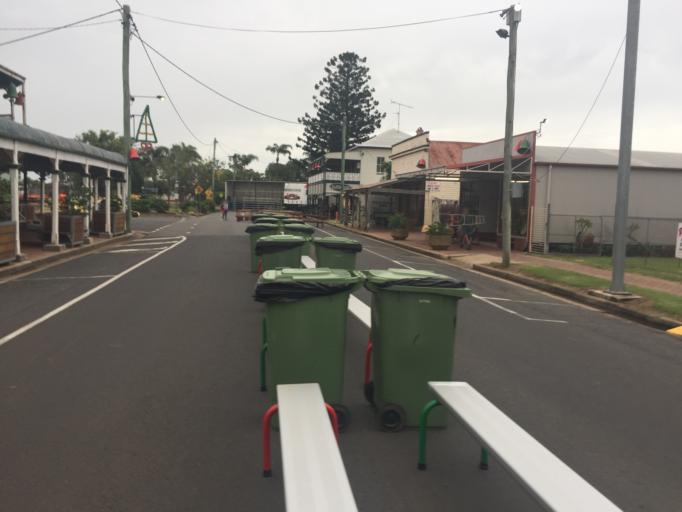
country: AU
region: Queensland
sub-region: Lockyer Valley
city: Gatton
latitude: -27.5898
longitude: 152.3567
